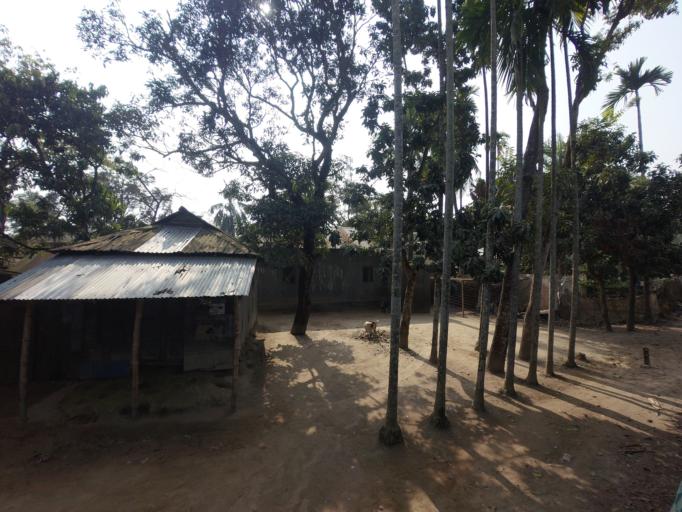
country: BD
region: Dhaka
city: Netrakona
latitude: 25.0096
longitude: 90.6449
